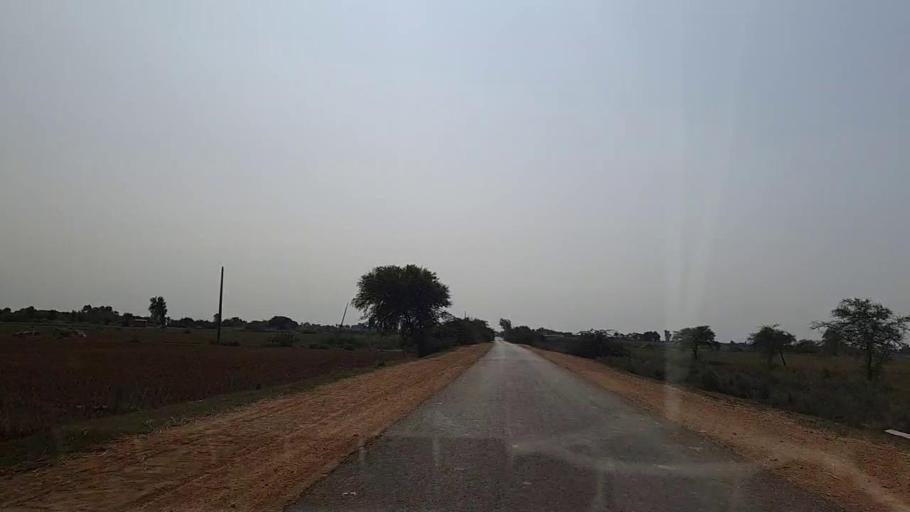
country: PK
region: Sindh
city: Chuhar Jamali
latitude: 24.3151
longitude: 67.9398
